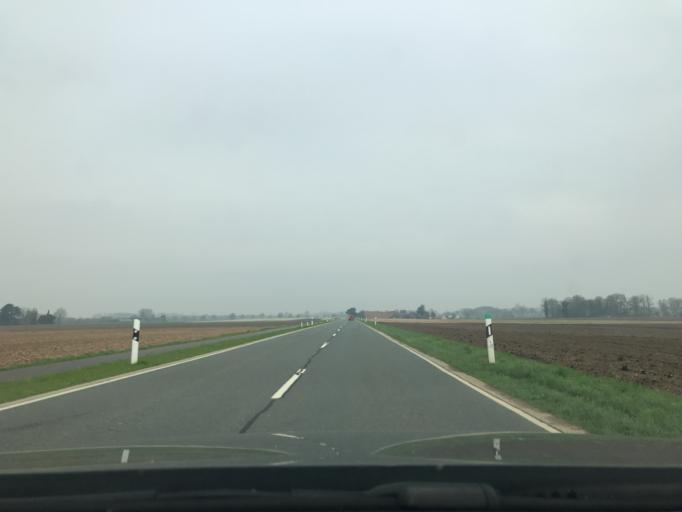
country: DE
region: North Rhine-Westphalia
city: Geldern
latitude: 51.4796
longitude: 6.3234
